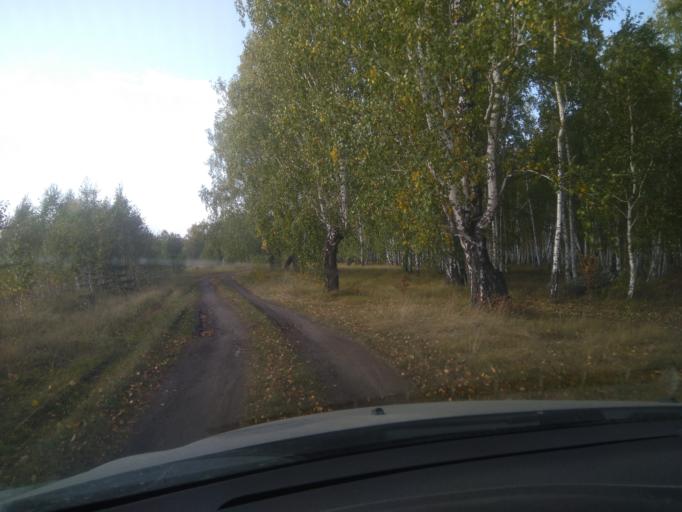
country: RU
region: Sverdlovsk
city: Pokrovskoye
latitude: 56.4284
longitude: 61.6102
